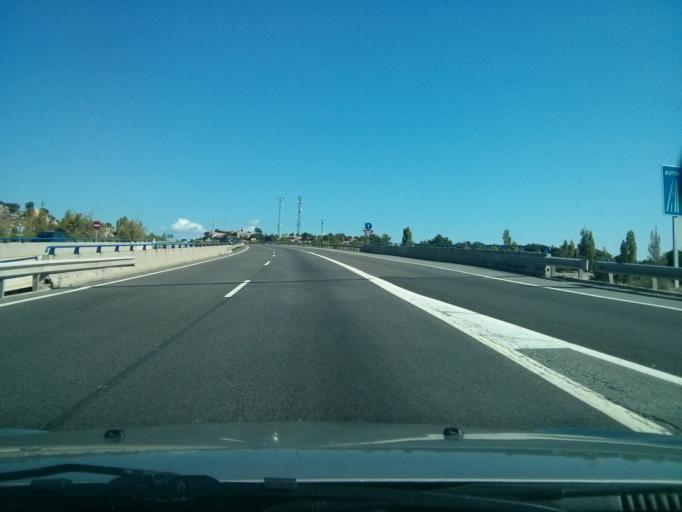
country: ES
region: Madrid
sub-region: Provincia de Madrid
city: La Cabrera
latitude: 40.8736
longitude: -3.6020
